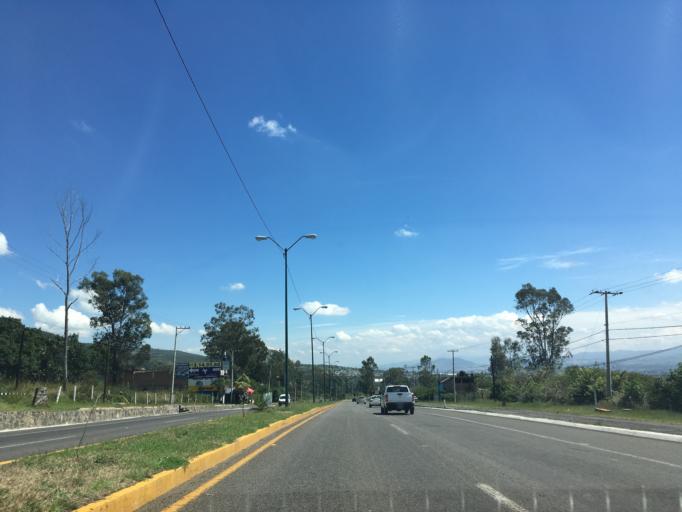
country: MX
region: Michoacan
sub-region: Morelia
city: Villa Magna
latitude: 19.6855
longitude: -101.3265
